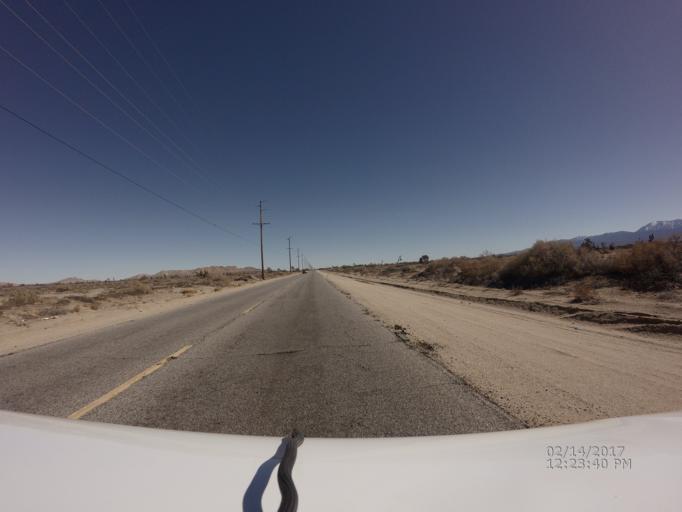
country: US
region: California
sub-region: Los Angeles County
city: Littlerock
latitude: 34.5798
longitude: -117.9137
